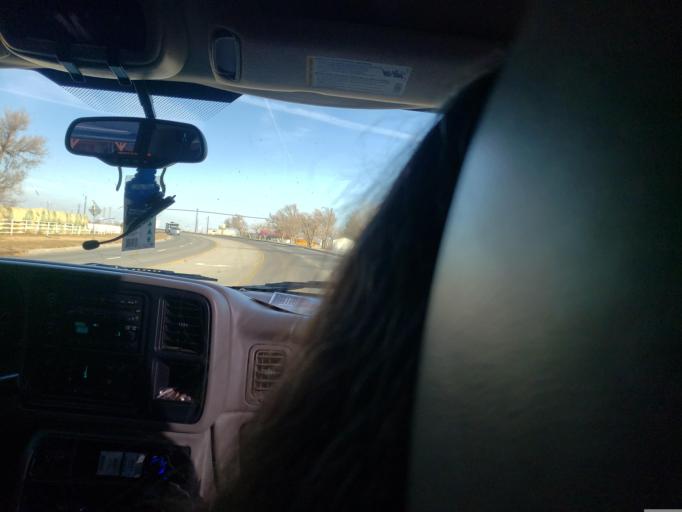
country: US
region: Oklahoma
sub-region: Texas County
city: Goodwell
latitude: 36.5016
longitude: -101.7808
